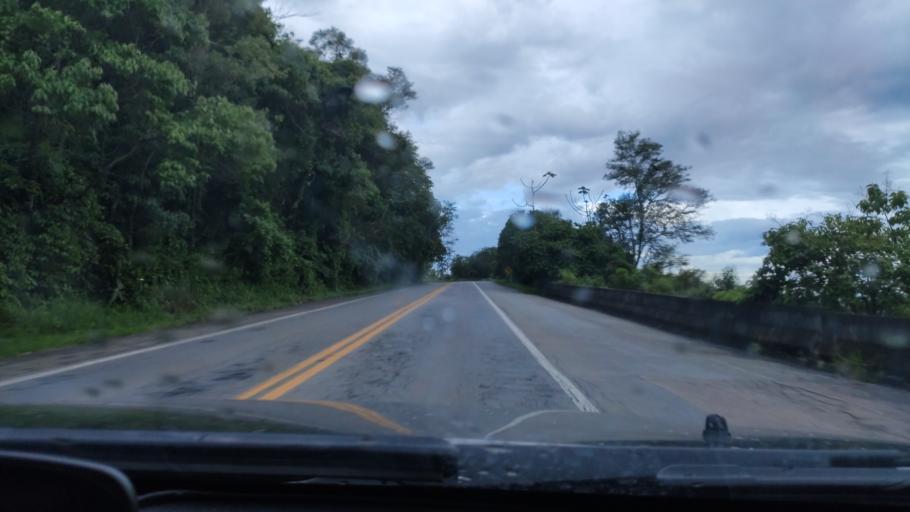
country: BR
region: Sao Paulo
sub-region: Braganca Paulista
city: Braganca Paulista
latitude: -22.8223
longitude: -46.5525
